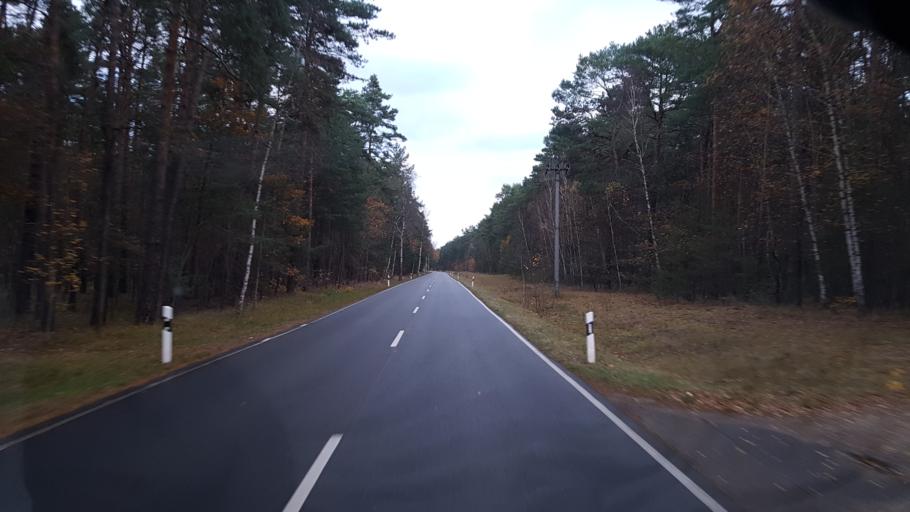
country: DE
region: Brandenburg
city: Ortrand
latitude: 51.3878
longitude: 13.7633
